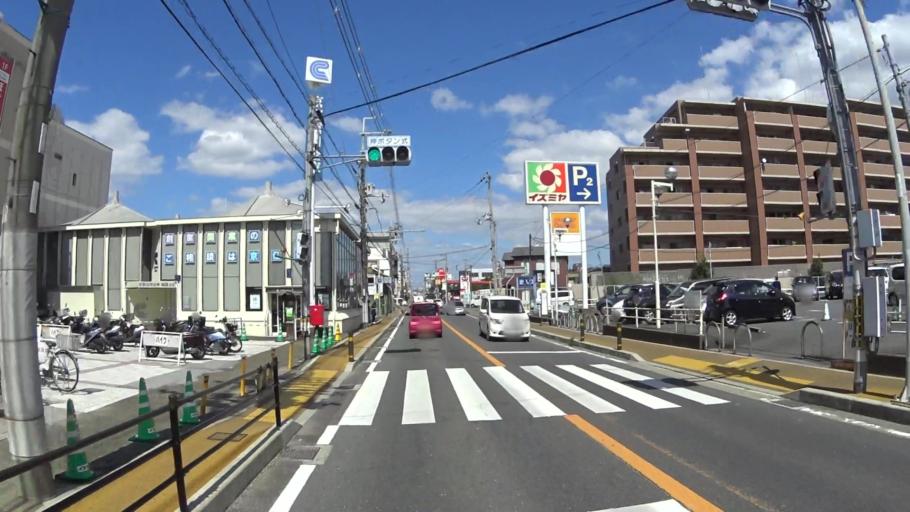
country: JP
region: Kyoto
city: Uji
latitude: 34.8679
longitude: 135.7773
